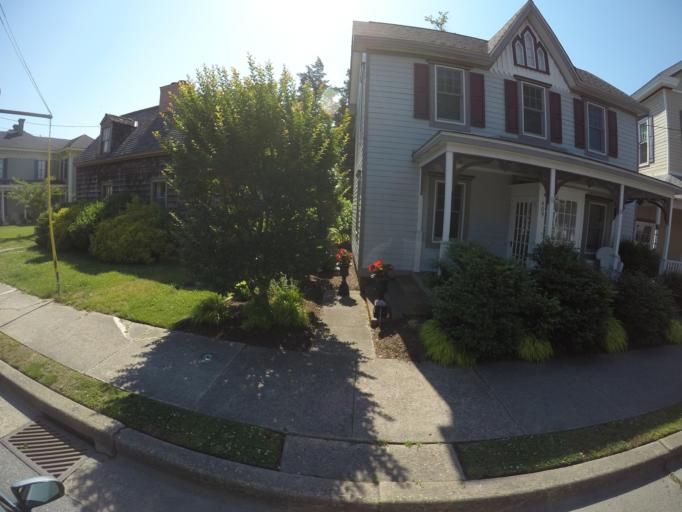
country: US
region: Delaware
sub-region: Sussex County
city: Lewes
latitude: 38.7710
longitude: -75.1406
